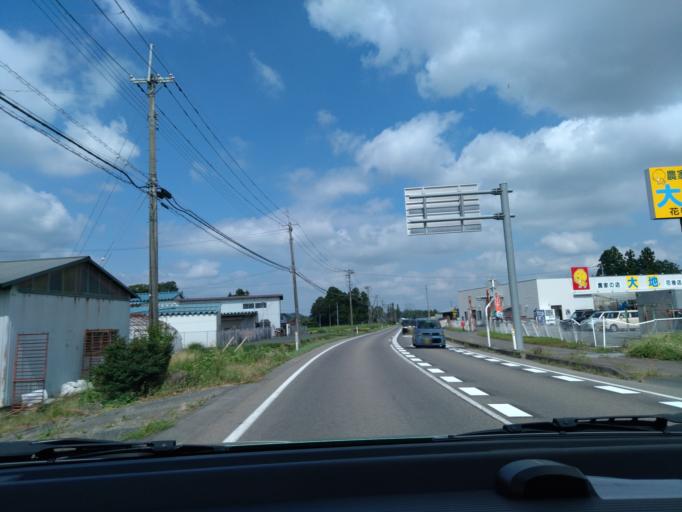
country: JP
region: Iwate
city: Hanamaki
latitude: 39.4519
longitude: 141.0978
